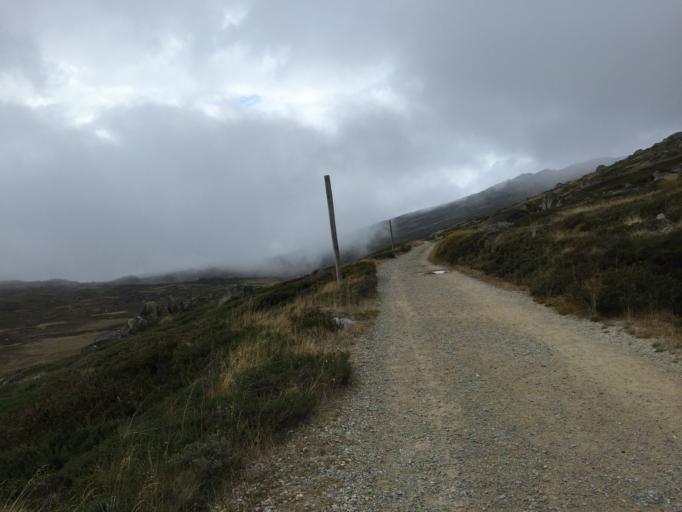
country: AU
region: New South Wales
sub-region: Snowy River
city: Jindabyne
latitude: -36.4550
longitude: 148.3026
